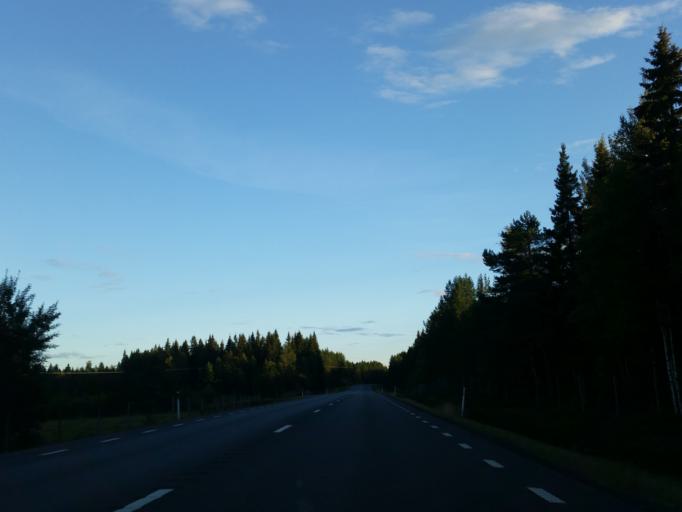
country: SE
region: Vaesterbotten
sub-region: Robertsfors Kommun
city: Robertsfors
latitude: 64.0294
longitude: 20.8415
